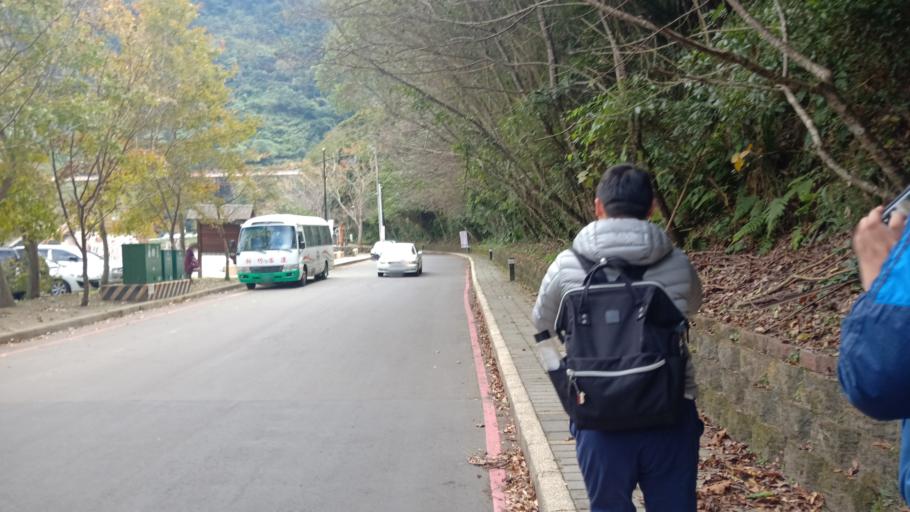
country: TW
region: Taiwan
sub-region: Hsinchu
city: Hsinchu
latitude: 24.5755
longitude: 121.1038
